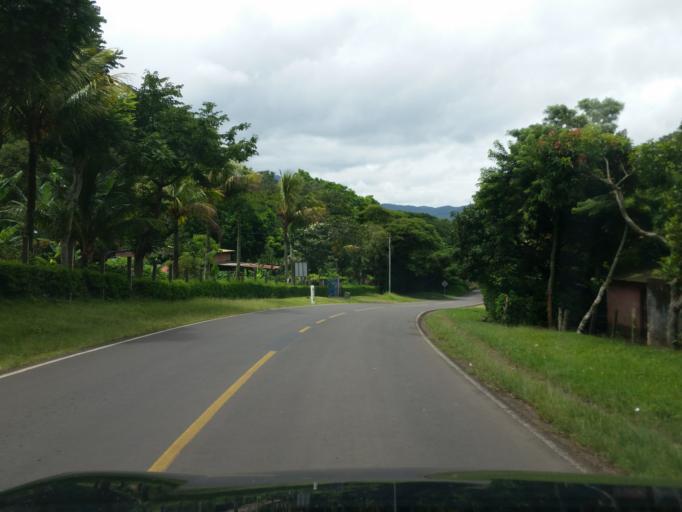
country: NI
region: Matagalpa
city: San Ramon
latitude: 12.9585
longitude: -85.8704
